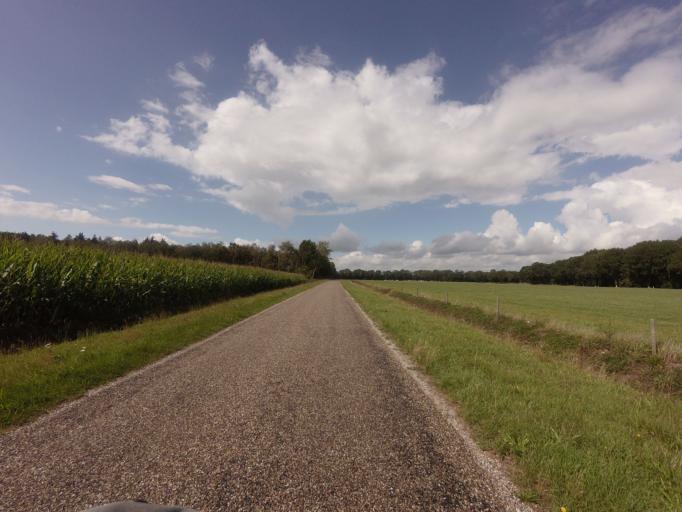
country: NL
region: Friesland
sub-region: Gemeente Heerenveen
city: Jubbega
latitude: 52.9768
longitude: 6.2710
